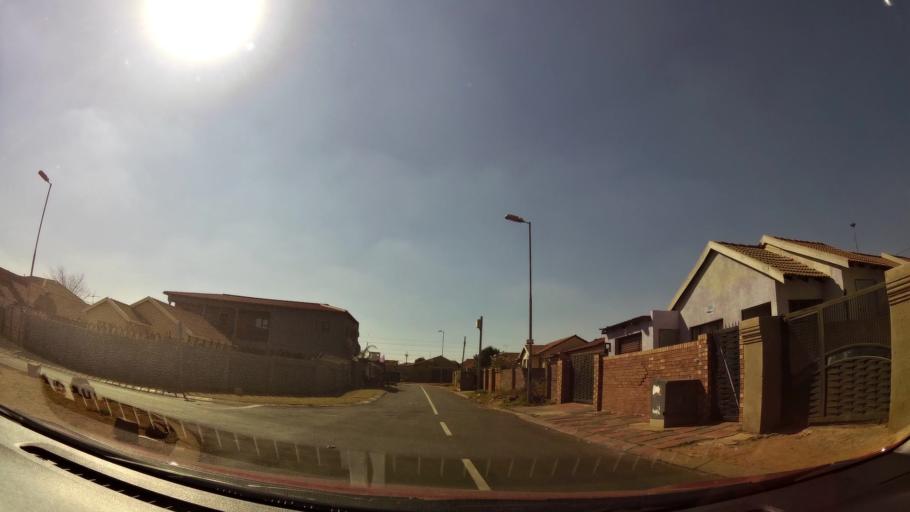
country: ZA
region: Gauteng
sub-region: City of Johannesburg Metropolitan Municipality
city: Soweto
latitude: -26.2372
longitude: 27.8201
